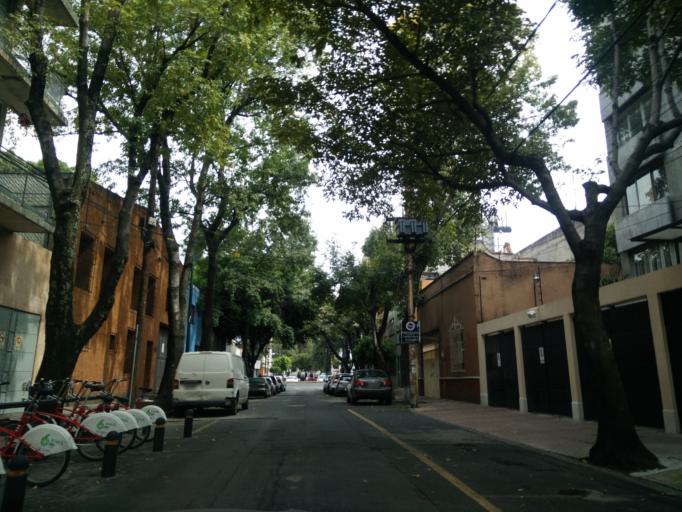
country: MX
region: Mexico City
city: Polanco
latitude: 19.4128
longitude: -99.1829
